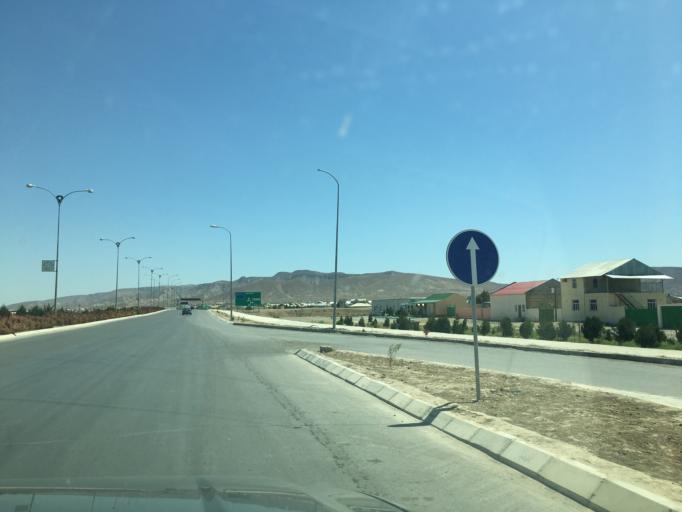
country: TM
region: Balkan
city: Serdar
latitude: 38.9861
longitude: 56.2913
